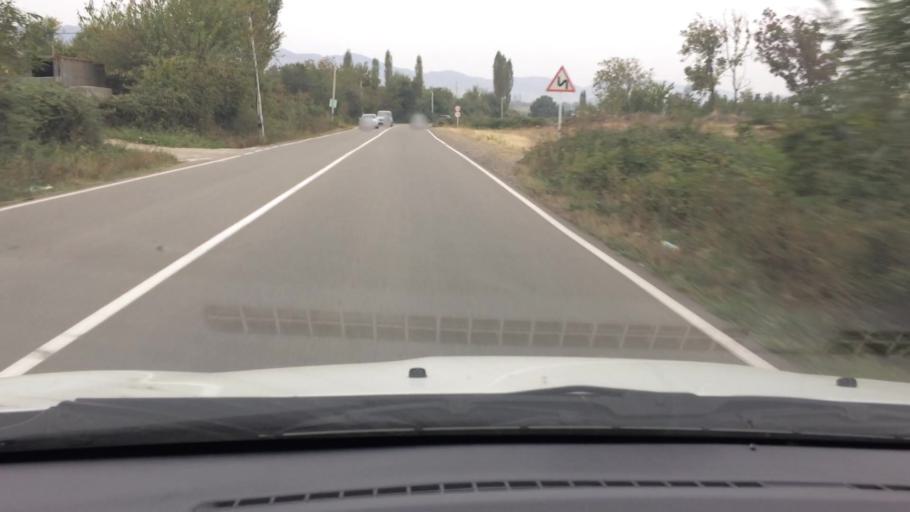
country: AM
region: Tavush
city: Bagratashen
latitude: 41.2622
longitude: 44.7954
